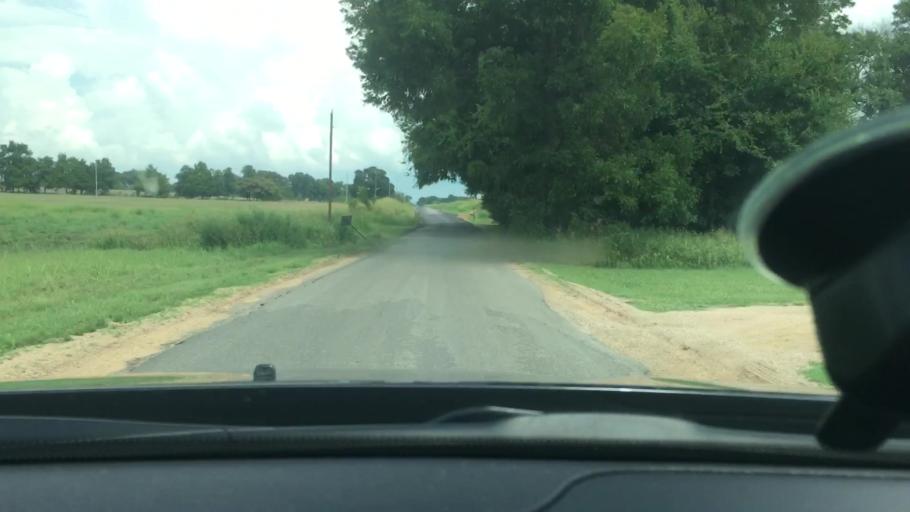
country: US
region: Oklahoma
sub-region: Carter County
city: Dickson
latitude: 34.2029
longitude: -96.8983
